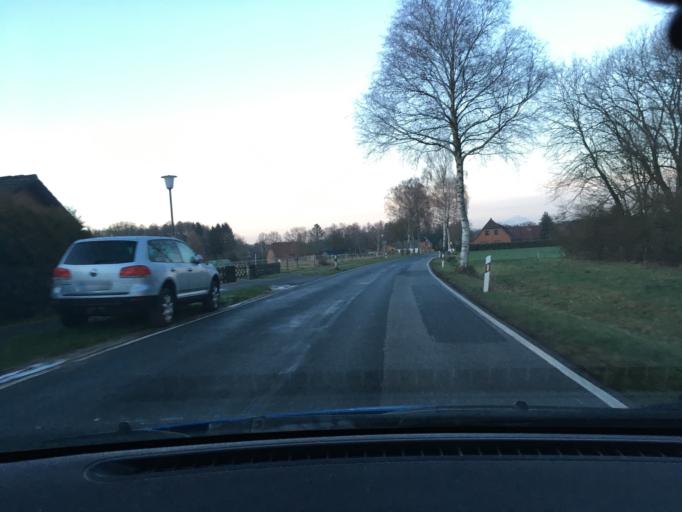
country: DE
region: Lower Saxony
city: Handeloh
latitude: 53.2588
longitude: 9.8820
